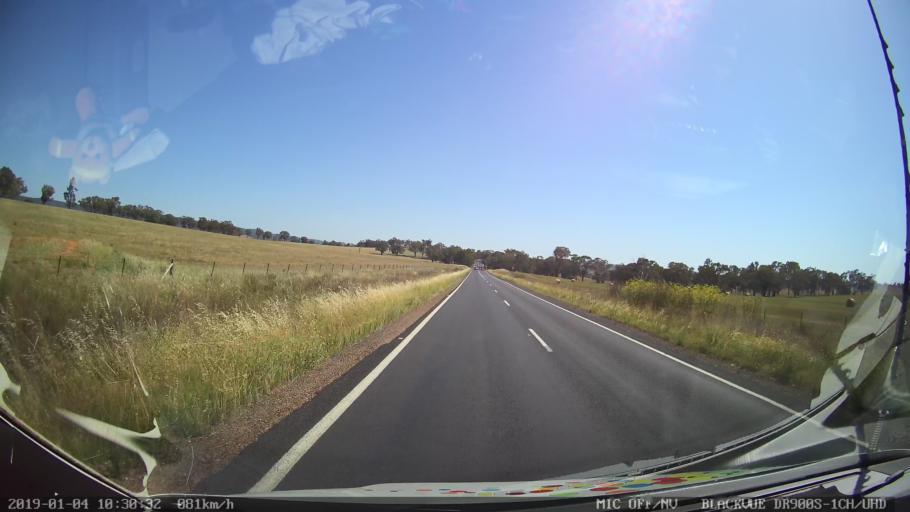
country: AU
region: New South Wales
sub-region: Cabonne
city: Canowindra
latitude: -33.3446
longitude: 148.6284
